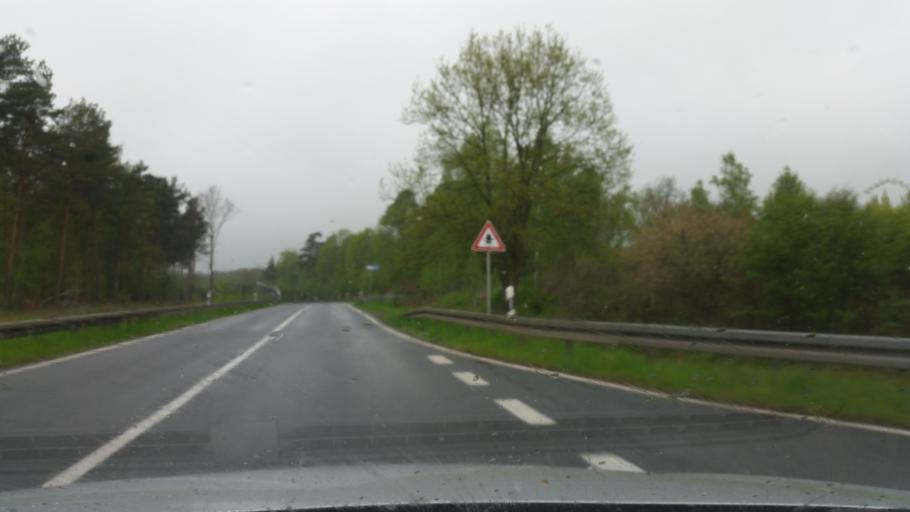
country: DE
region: Saxony-Anhalt
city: Harbke
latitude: 52.2193
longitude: 11.0517
